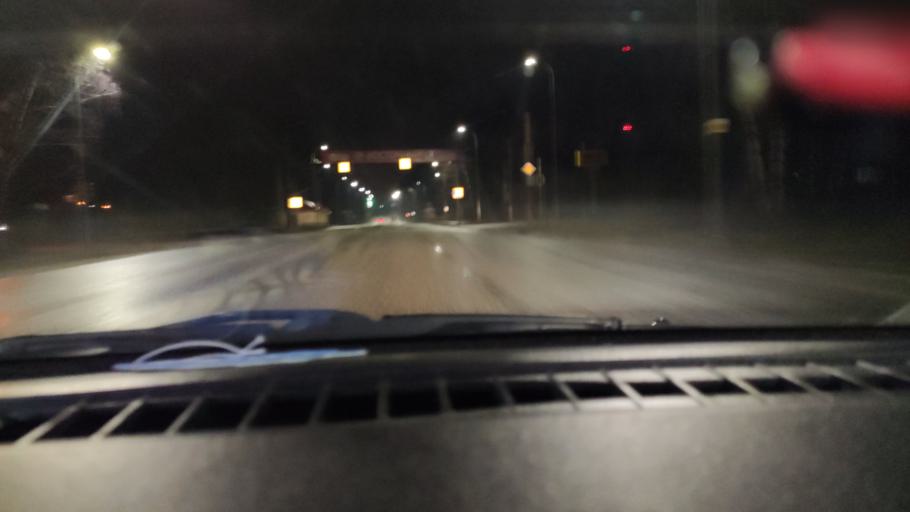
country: RU
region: Udmurtiya
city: Khokhryaki
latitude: 56.9189
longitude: 53.4712
